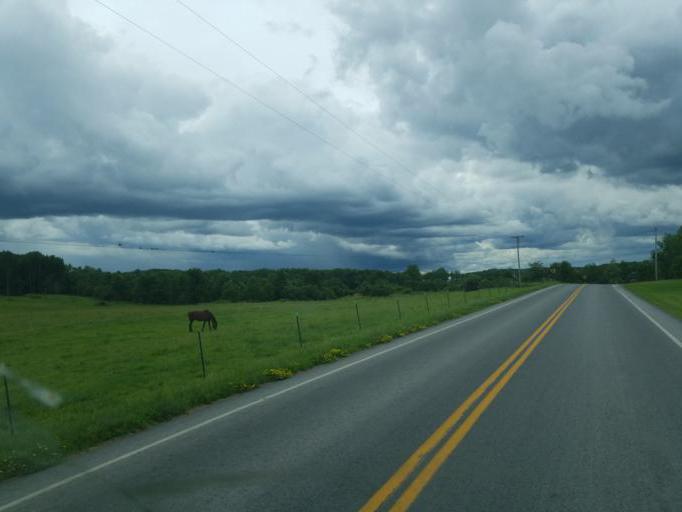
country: US
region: New York
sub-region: Wayne County
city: Lyons
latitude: 43.0243
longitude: -76.9286
